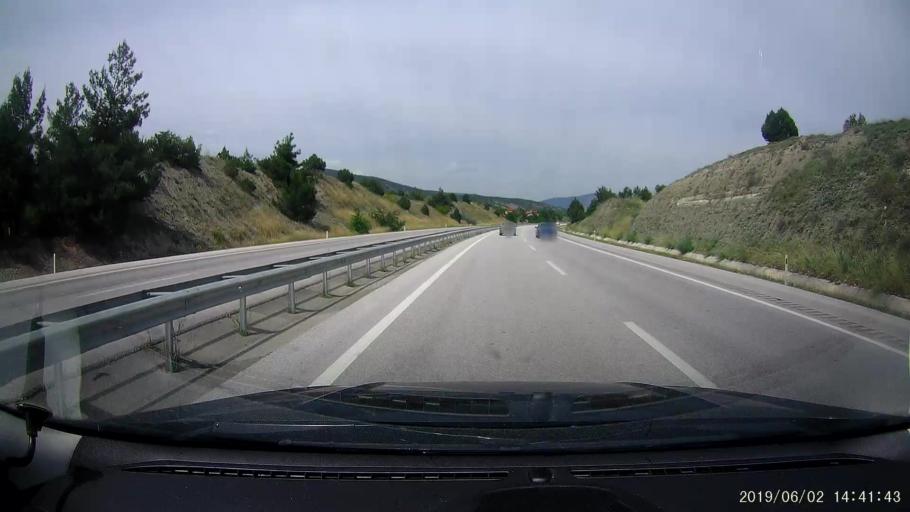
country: TR
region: Corum
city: Hacihamza
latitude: 41.0913
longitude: 34.3443
